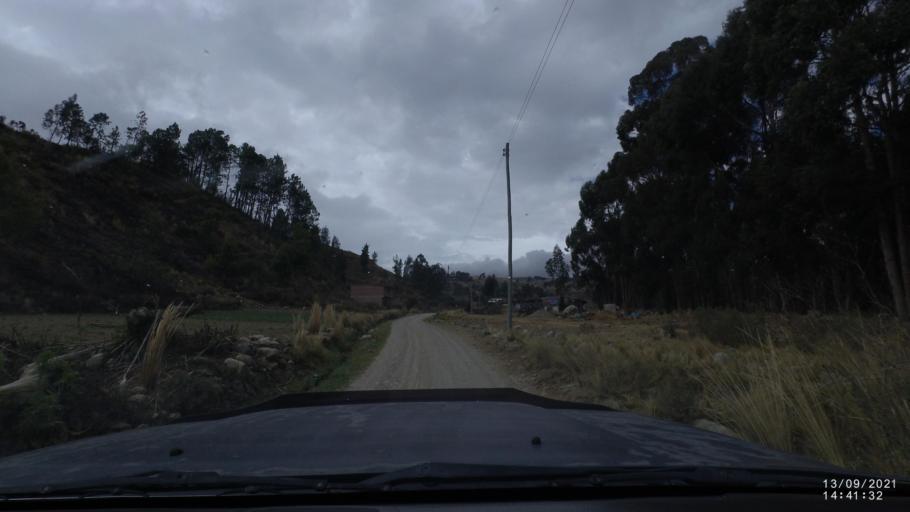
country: BO
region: Cochabamba
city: Colomi
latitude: -17.3678
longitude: -65.8181
